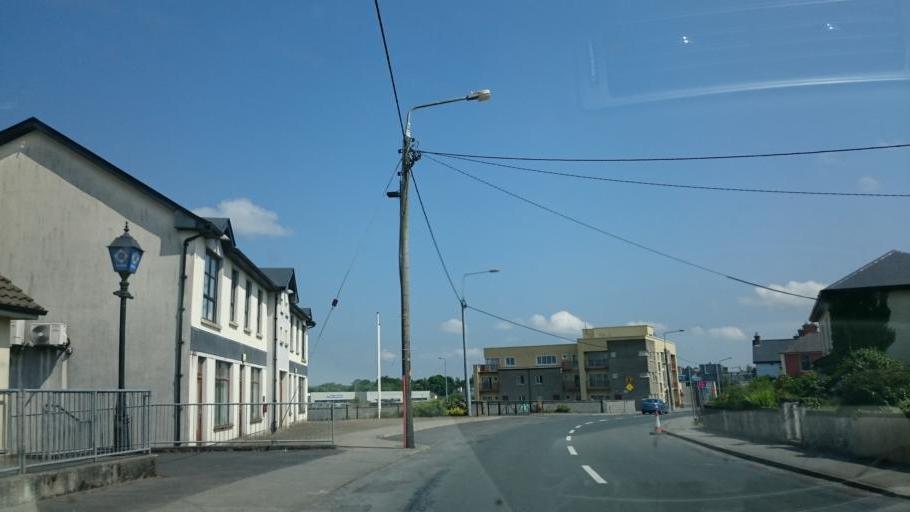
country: IE
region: Connaught
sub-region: Sligo
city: Tobercurry
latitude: 54.0514
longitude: -8.7342
